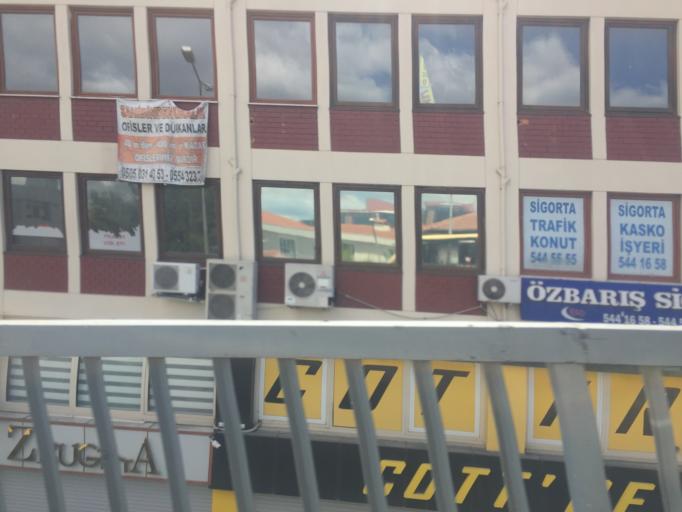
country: TR
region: Istanbul
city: merter keresteciler
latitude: 41.0304
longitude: 28.9151
